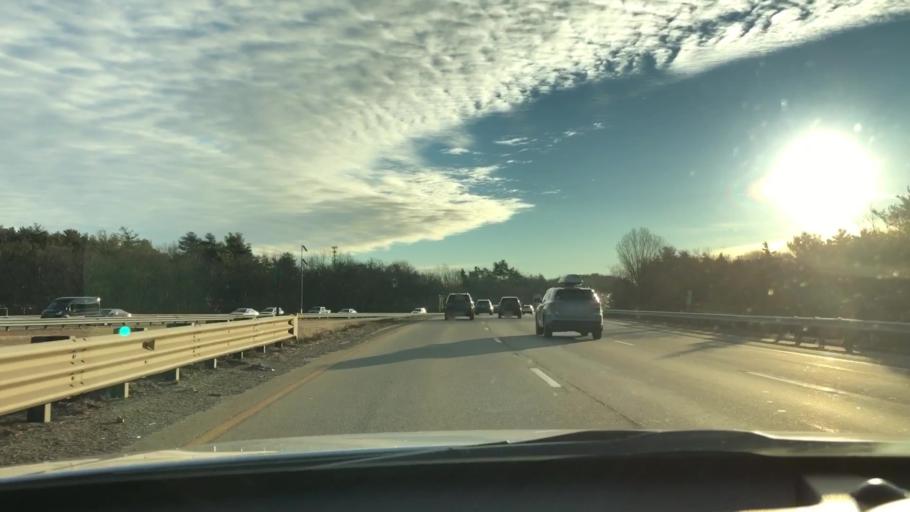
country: US
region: Massachusetts
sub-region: Norfolk County
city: Weymouth
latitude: 42.1859
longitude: -70.9341
